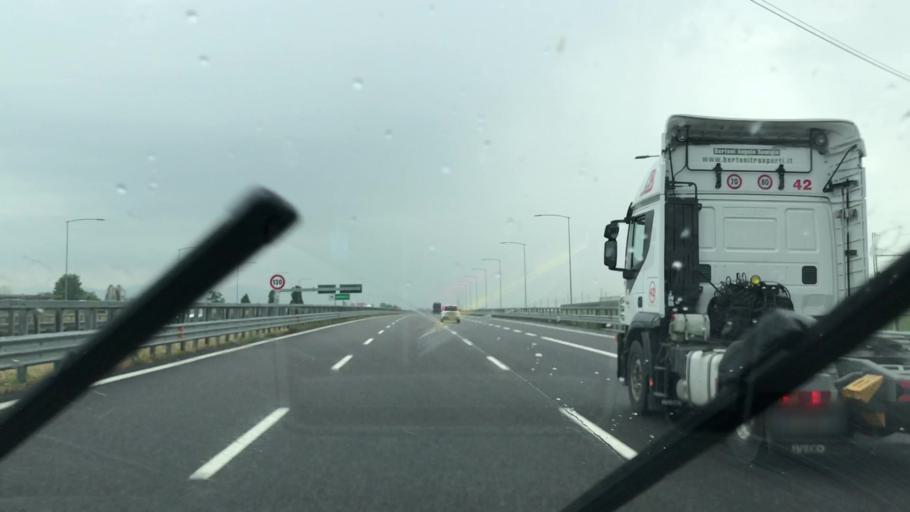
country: IT
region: Lombardy
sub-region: Provincia di Brescia
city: Chiari
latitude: 45.5163
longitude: 9.9233
